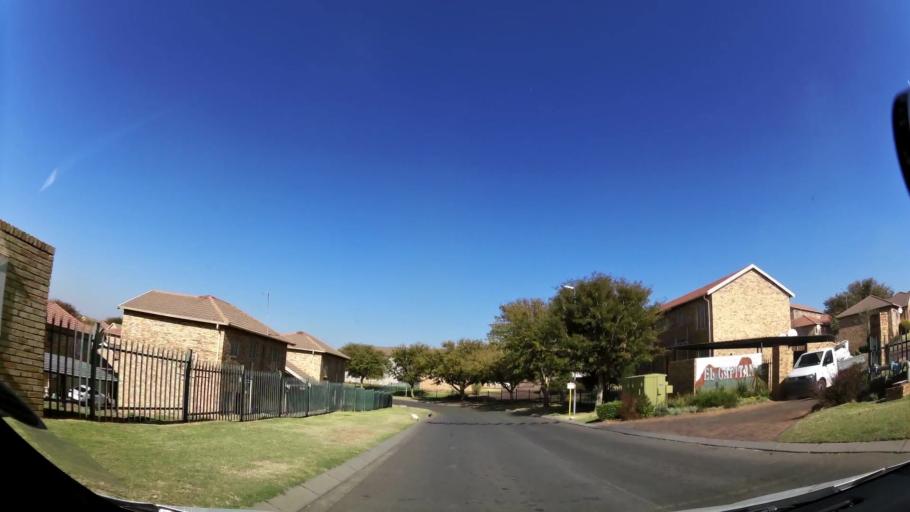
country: ZA
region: Gauteng
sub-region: Ekurhuleni Metropolitan Municipality
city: Germiston
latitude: -26.2476
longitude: 28.1136
